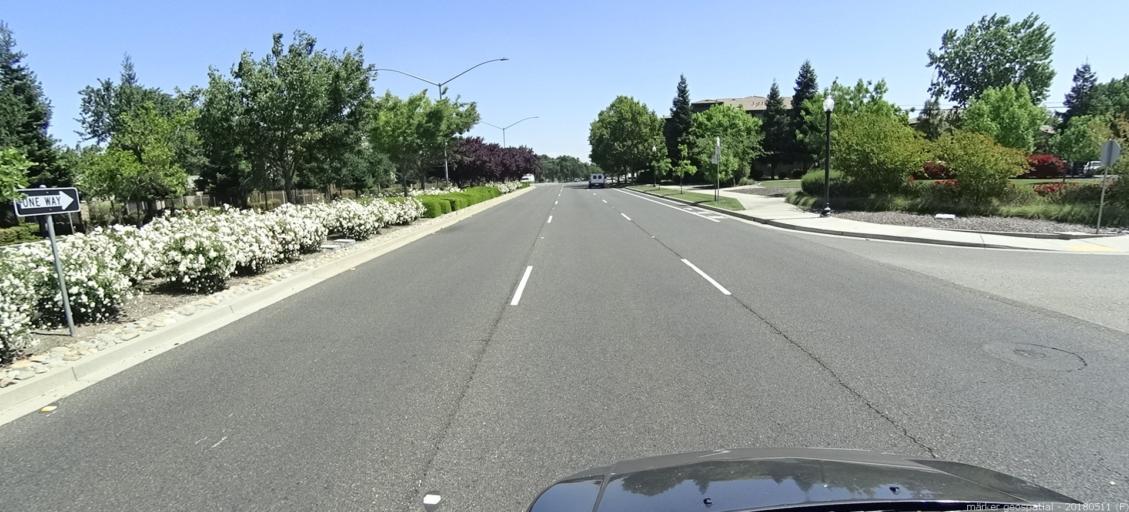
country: US
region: California
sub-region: Yolo County
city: West Sacramento
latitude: 38.6445
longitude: -121.5148
